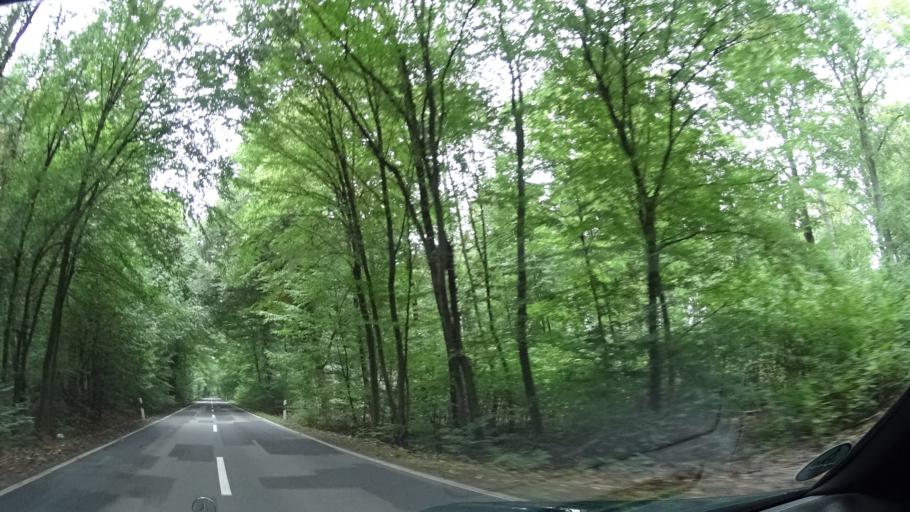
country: DE
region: Brandenburg
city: Walsleben
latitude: 52.9739
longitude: 12.7149
